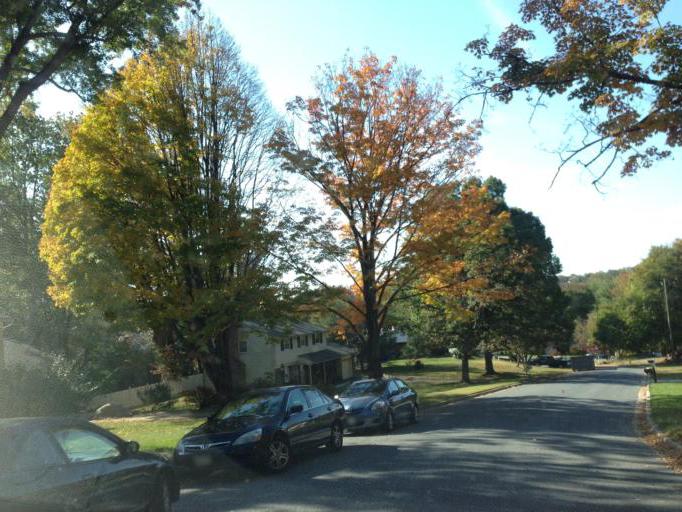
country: US
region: Maryland
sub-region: Howard County
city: Ellicott City
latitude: 39.2737
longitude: -76.8072
